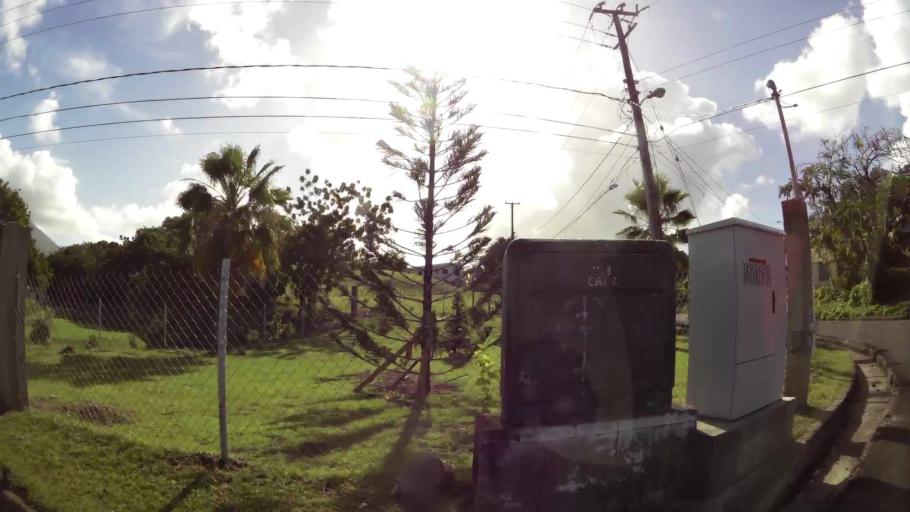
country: KN
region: Saint Paul Charlestown
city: Charlestown
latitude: 17.1324
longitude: -62.6274
